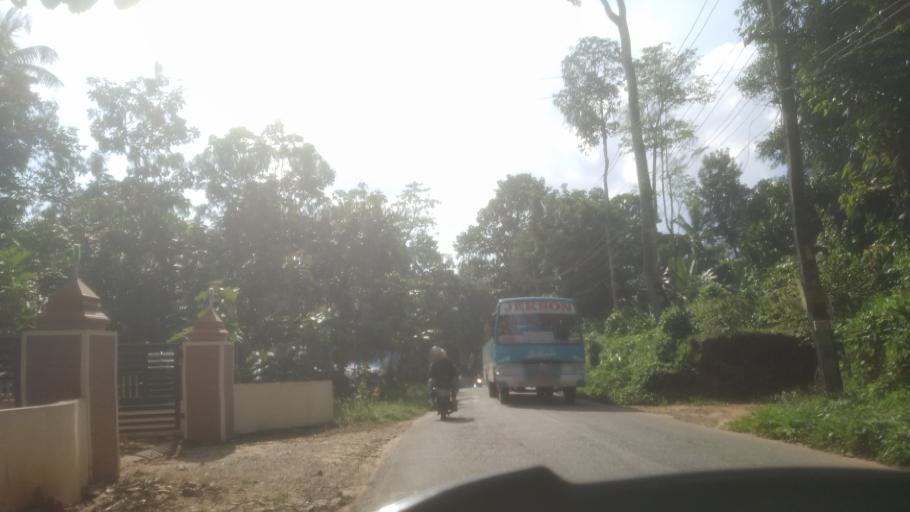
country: IN
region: Kerala
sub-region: Ernakulam
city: Muvattupula
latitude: 9.9995
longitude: 76.6322
